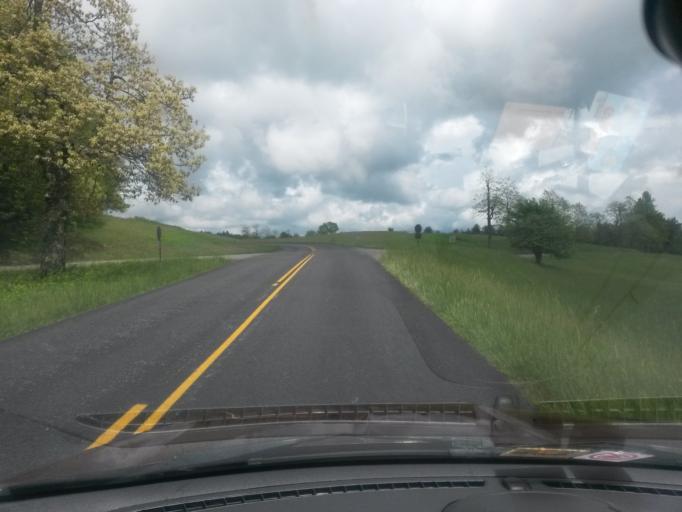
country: US
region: Virginia
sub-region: Floyd County
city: Floyd
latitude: 36.7989
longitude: -80.3825
